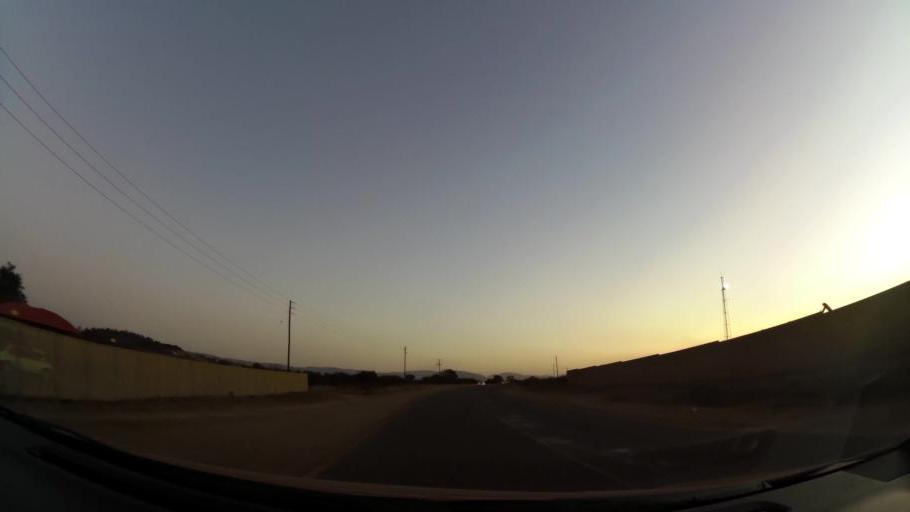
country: ZA
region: North-West
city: Ga-Rankuwa
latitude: -25.6282
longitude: 27.9620
